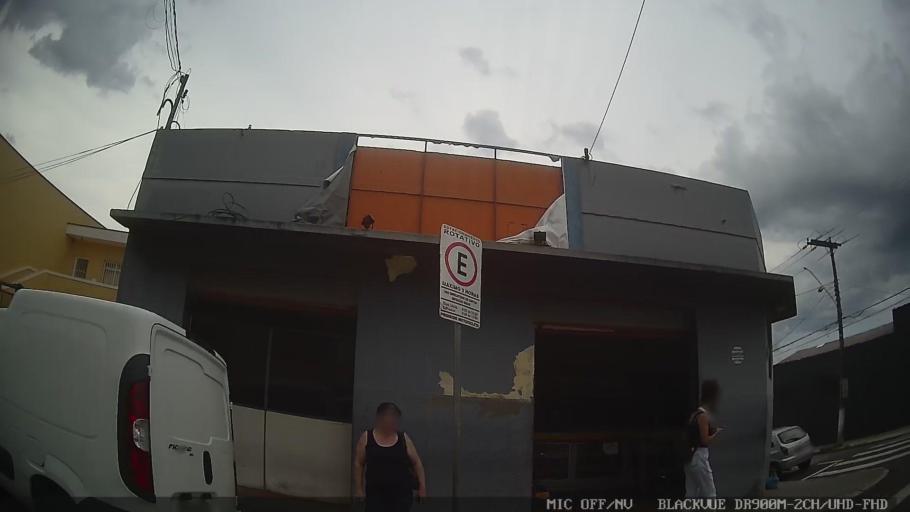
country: BR
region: Sao Paulo
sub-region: Atibaia
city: Atibaia
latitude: -23.1134
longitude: -46.5582
